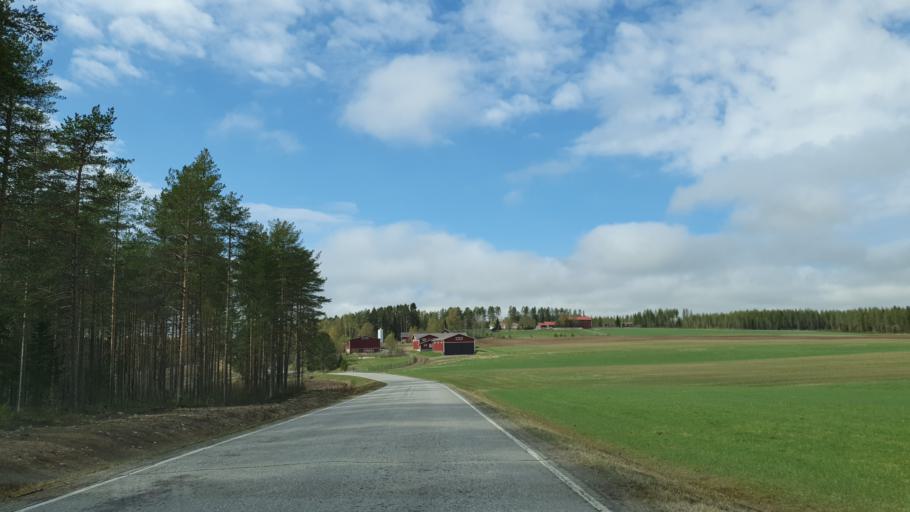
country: FI
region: Kainuu
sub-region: Kehys-Kainuu
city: Kuhmo
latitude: 64.1238
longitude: 29.6542
